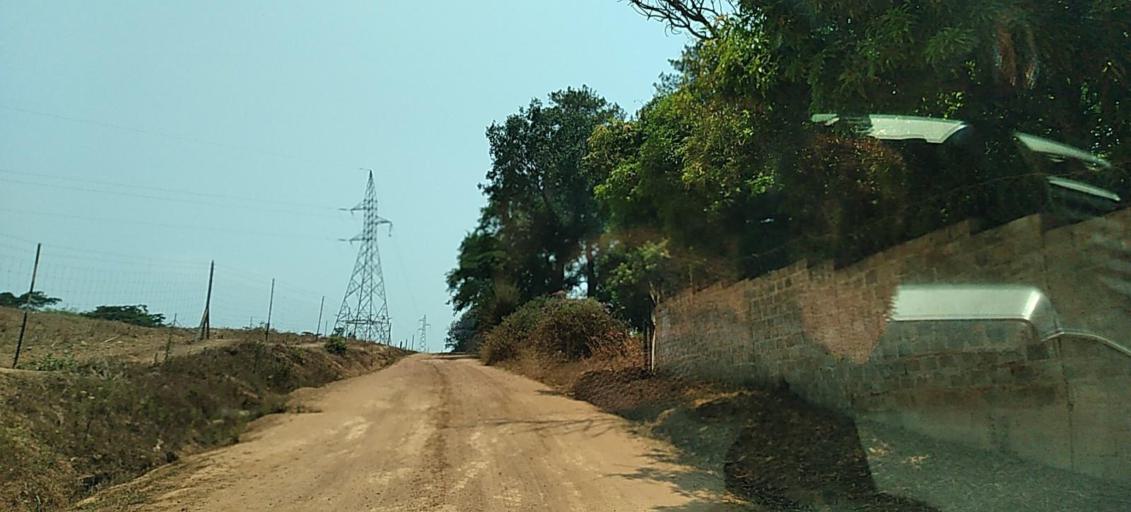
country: ZM
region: Copperbelt
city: Chambishi
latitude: -12.6218
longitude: 27.9450
